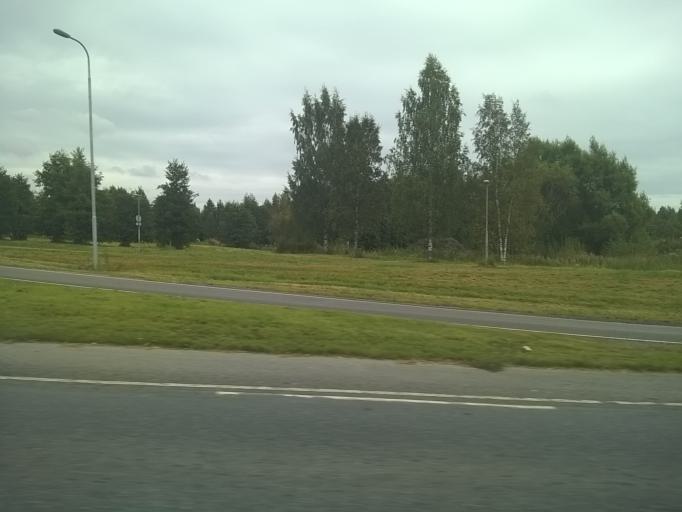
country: FI
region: Pirkanmaa
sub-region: Tampere
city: Tampere
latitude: 61.4840
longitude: 23.8278
